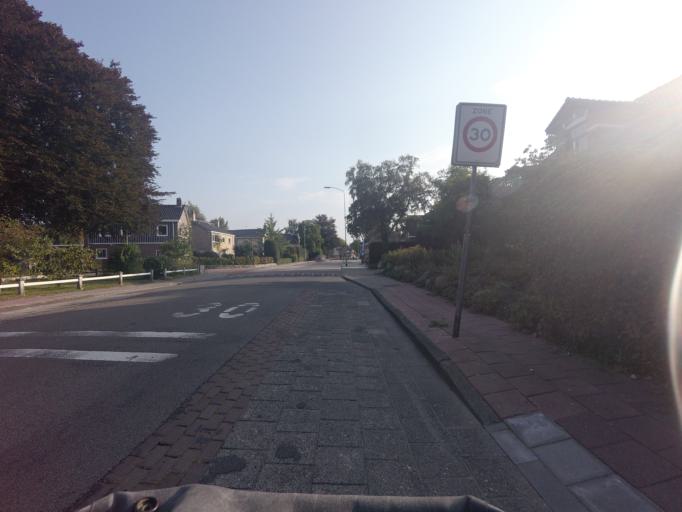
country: NL
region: Groningen
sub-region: Gemeente Haren
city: Haren
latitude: 53.1365
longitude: 6.5641
